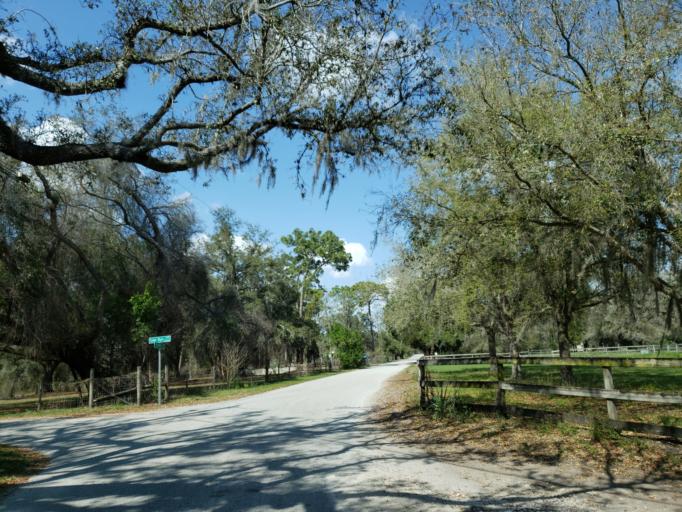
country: US
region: Florida
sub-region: Hillsborough County
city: Keystone
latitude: 28.1512
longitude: -82.6408
